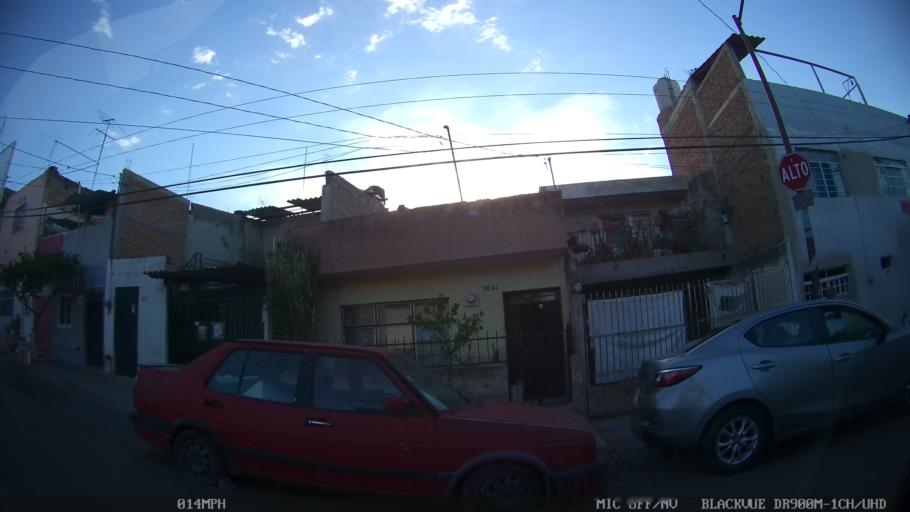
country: MX
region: Jalisco
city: Tlaquepaque
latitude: 20.7091
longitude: -103.3025
